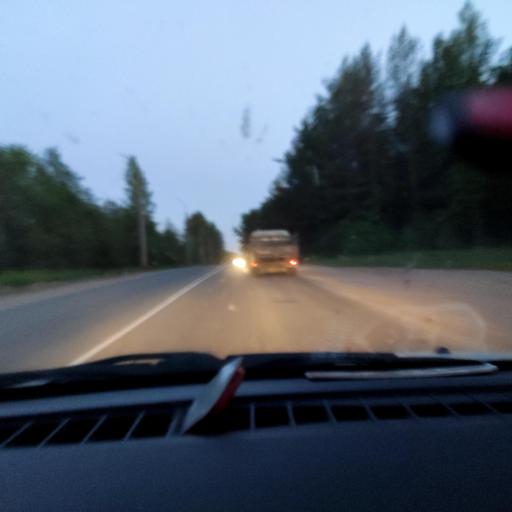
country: RU
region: Perm
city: Overyata
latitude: 58.0348
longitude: 55.8512
